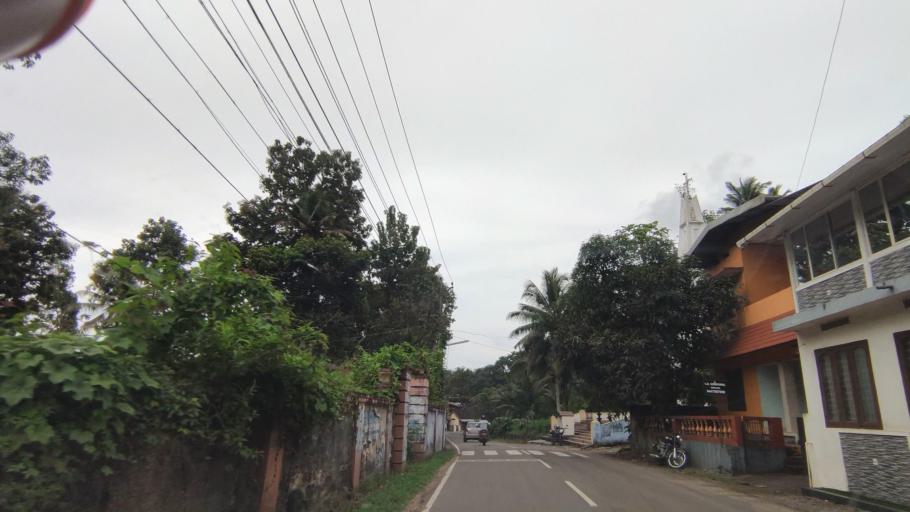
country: IN
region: Kerala
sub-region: Kottayam
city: Kottayam
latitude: 9.6456
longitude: 76.5182
